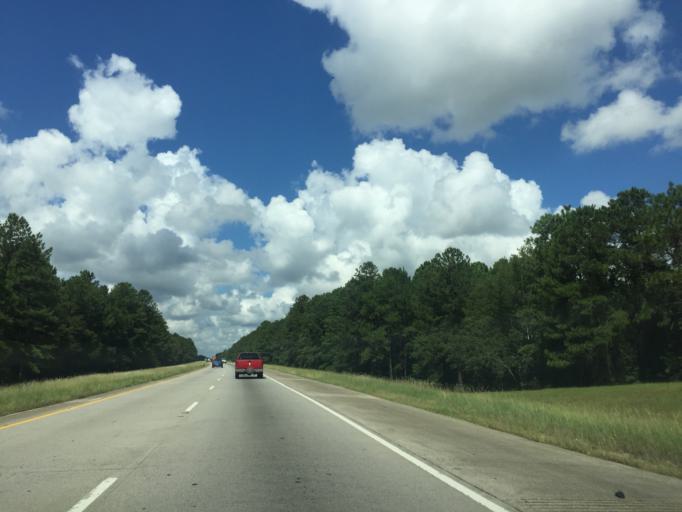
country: US
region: Georgia
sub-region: Candler County
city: Metter
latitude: 32.3795
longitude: -82.1921
